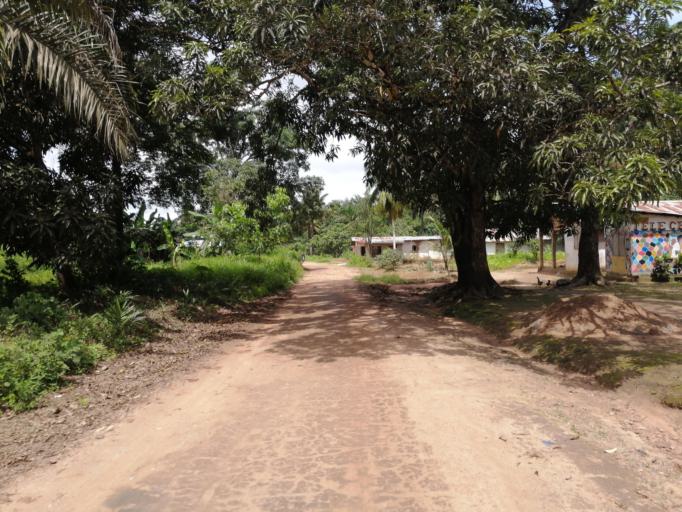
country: SL
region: Northern Province
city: Pepel
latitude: 8.6128
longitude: -13.0488
